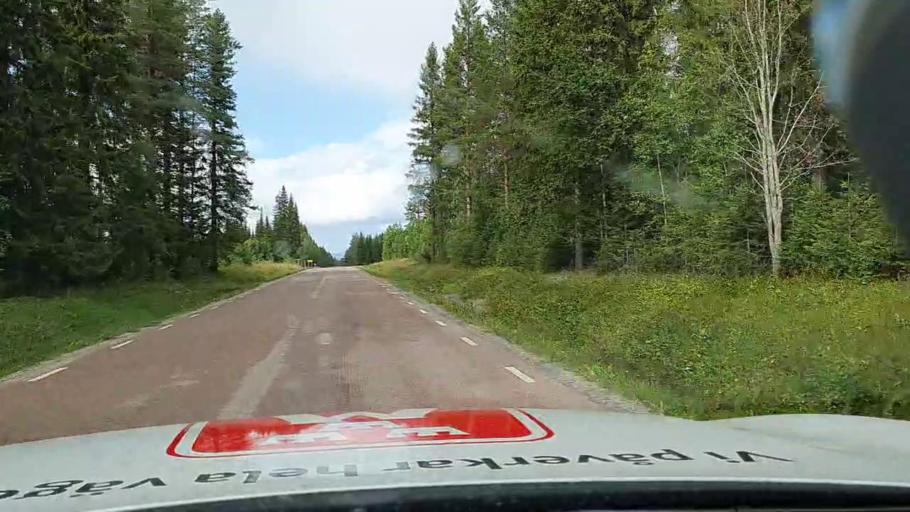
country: SE
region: Jaemtland
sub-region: Stroemsunds Kommun
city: Stroemsund
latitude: 63.8700
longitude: 15.3712
